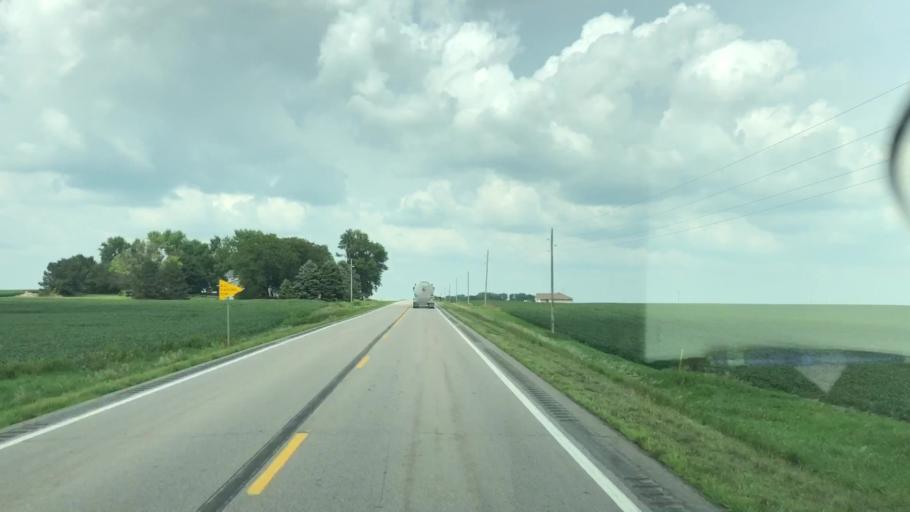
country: US
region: Iowa
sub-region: Plymouth County
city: Remsen
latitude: 42.7890
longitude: -95.9578
